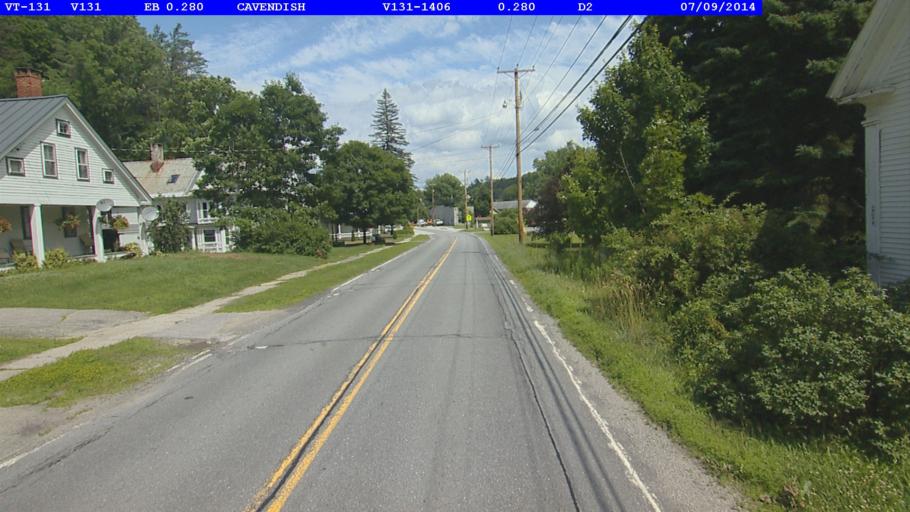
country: US
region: Vermont
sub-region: Windsor County
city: Chester
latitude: 43.3818
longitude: -72.6417
